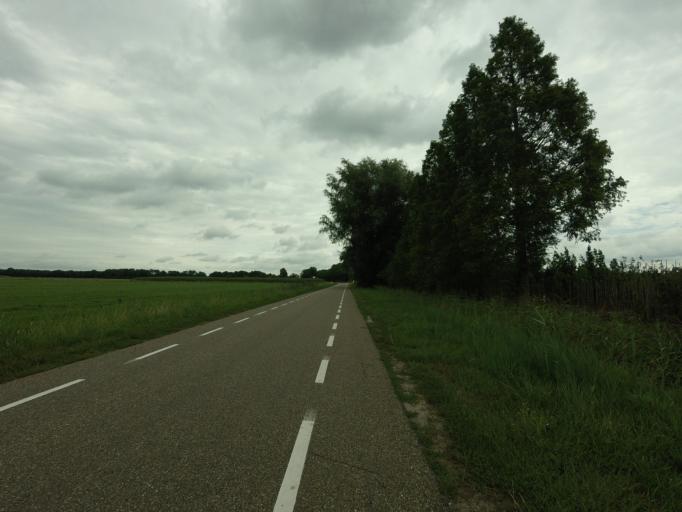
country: NL
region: Gelderland
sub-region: Gemeente Lochem
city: Laren
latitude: 52.2900
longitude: 6.3506
